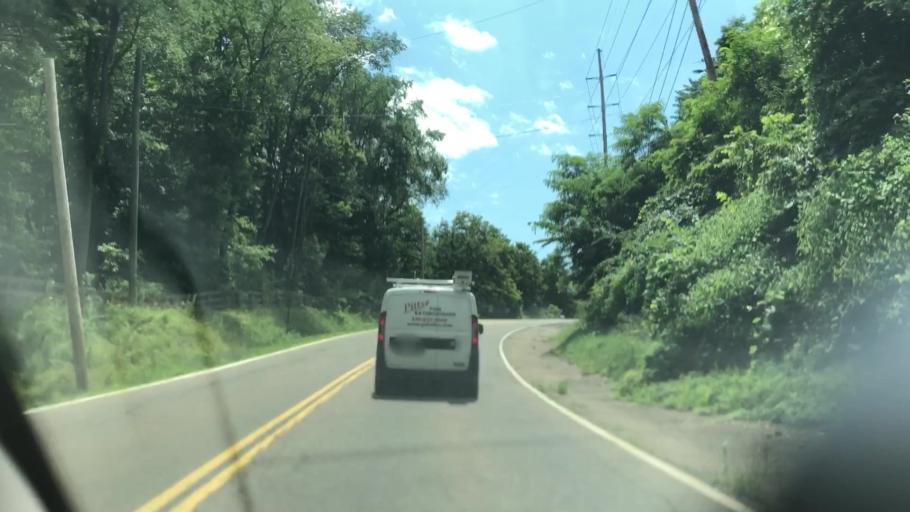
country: US
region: Ohio
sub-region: Summit County
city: Greensburg
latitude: 40.9075
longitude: -81.4972
